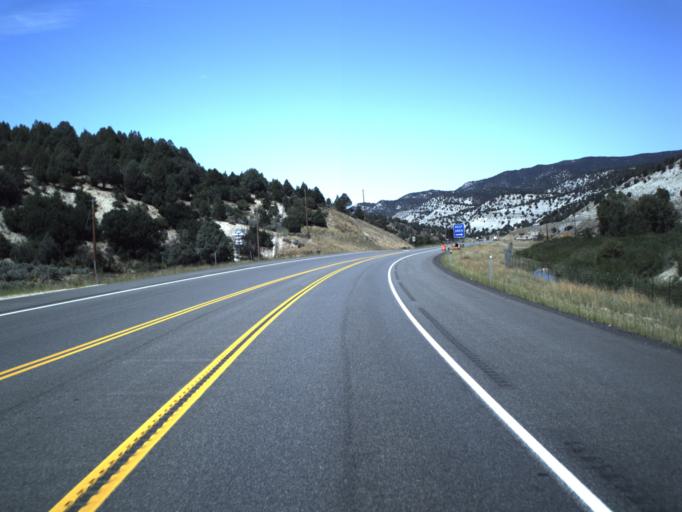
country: US
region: Utah
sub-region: Sanpete County
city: Fairview
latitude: 39.9476
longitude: -111.2125
